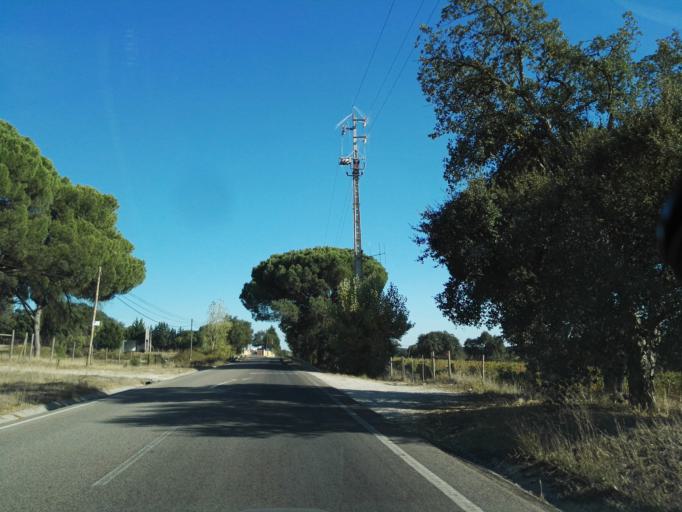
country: PT
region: Santarem
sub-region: Benavente
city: Poceirao
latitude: 38.8505
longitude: -8.7195
